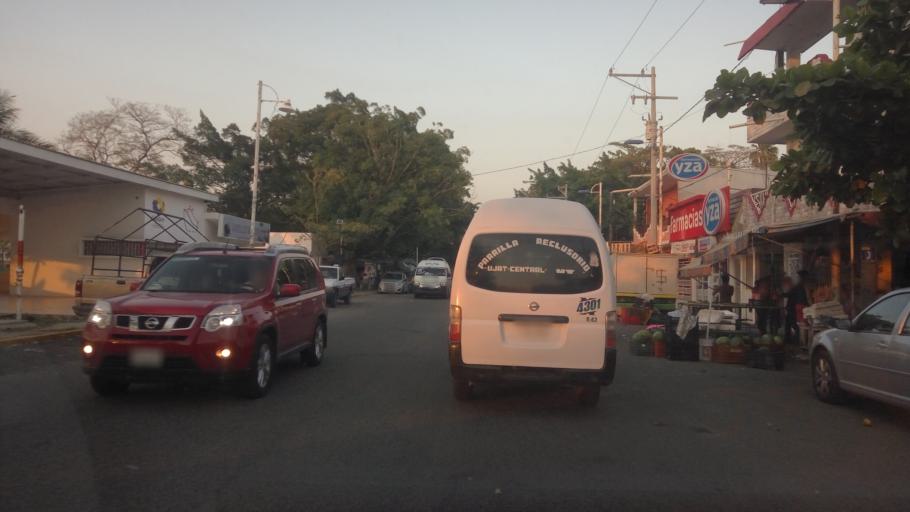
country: MX
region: Tabasco
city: Villahermosa
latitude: 17.9848
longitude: -92.9184
